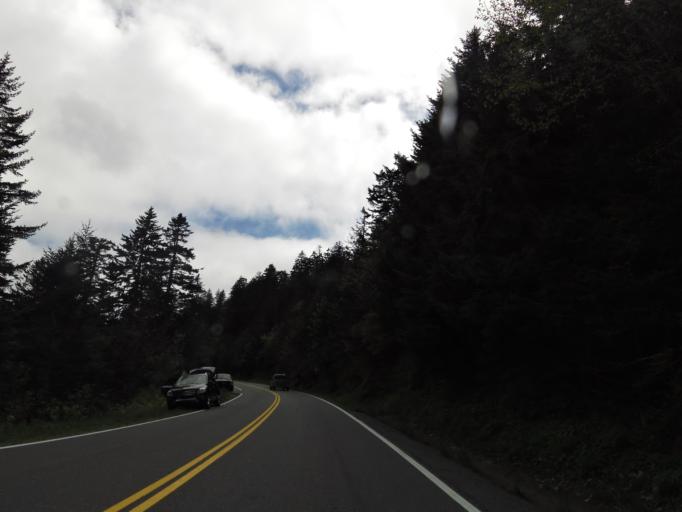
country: US
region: North Carolina
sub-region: Swain County
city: Bryson City
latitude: 35.5605
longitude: -83.4935
